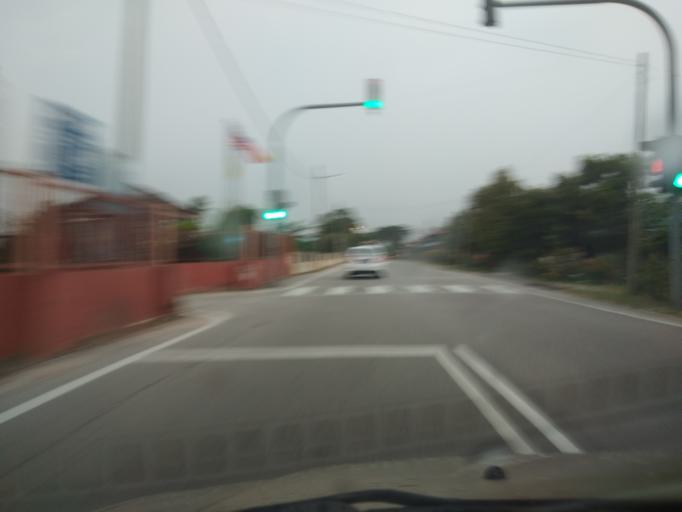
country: MY
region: Penang
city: Permatang Kuching
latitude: 5.4784
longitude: 100.4014
